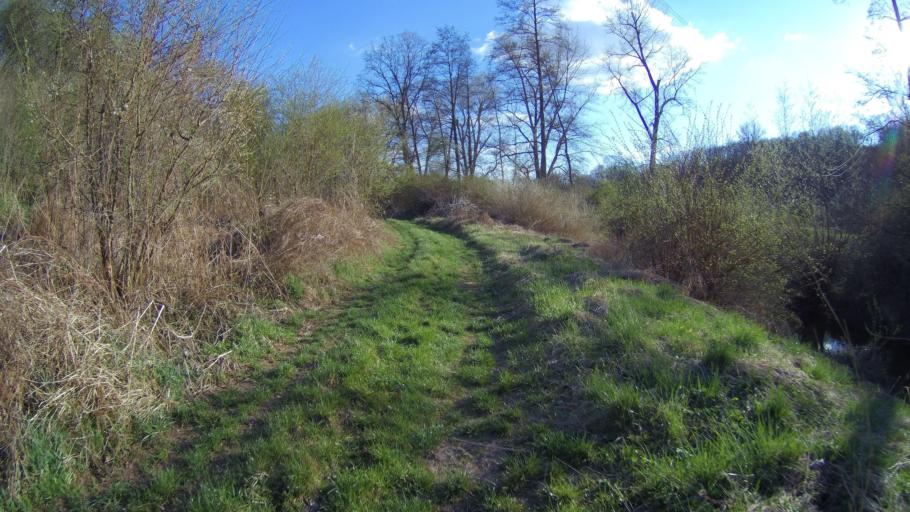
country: CZ
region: Ustecky
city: Zatec
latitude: 50.3113
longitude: 13.5976
